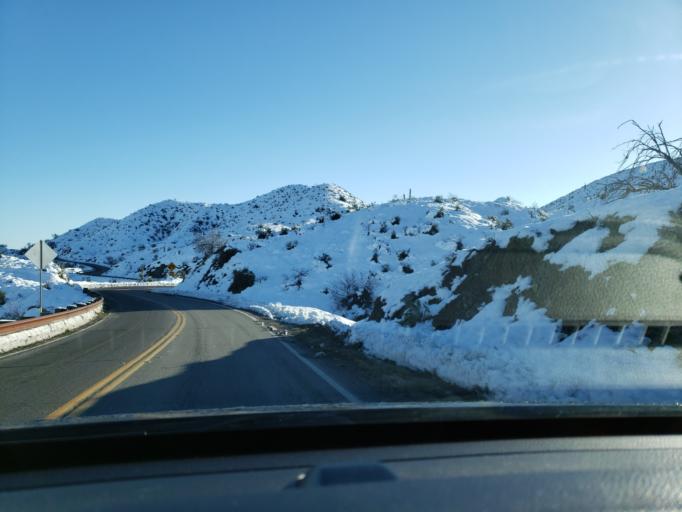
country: US
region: Arizona
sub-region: Maricopa County
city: Carefree
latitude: 33.8921
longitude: -111.8197
